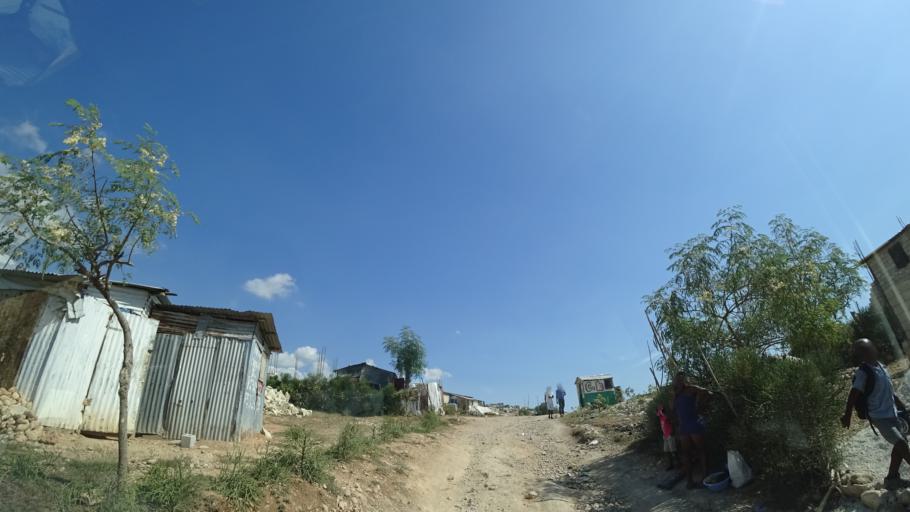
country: HT
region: Ouest
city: Croix des Bouquets
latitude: 18.6594
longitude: -72.2854
